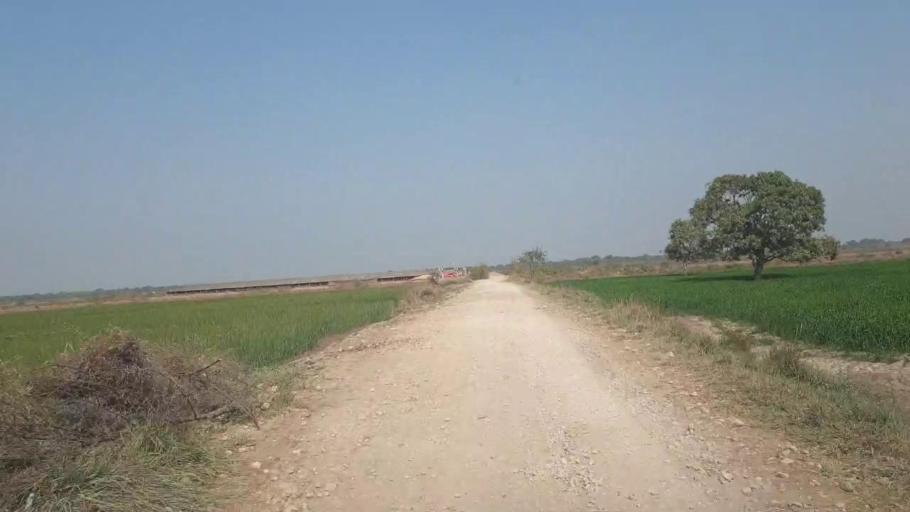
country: PK
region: Sindh
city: Tando Allahyar
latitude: 25.4385
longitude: 68.8359
